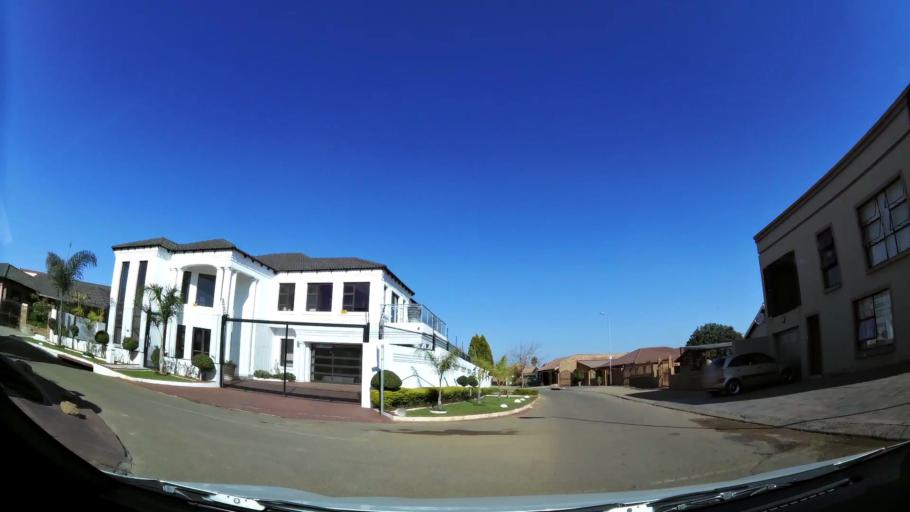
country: ZA
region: Gauteng
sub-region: City of Tshwane Metropolitan Municipality
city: Cullinan
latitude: -25.7181
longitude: 28.3778
